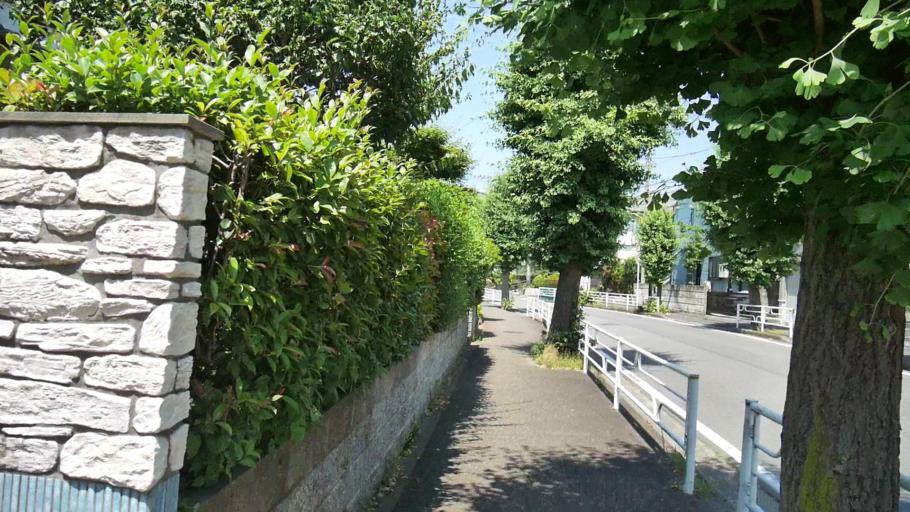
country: JP
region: Kanagawa
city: Fujisawa
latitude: 35.3980
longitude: 139.5185
